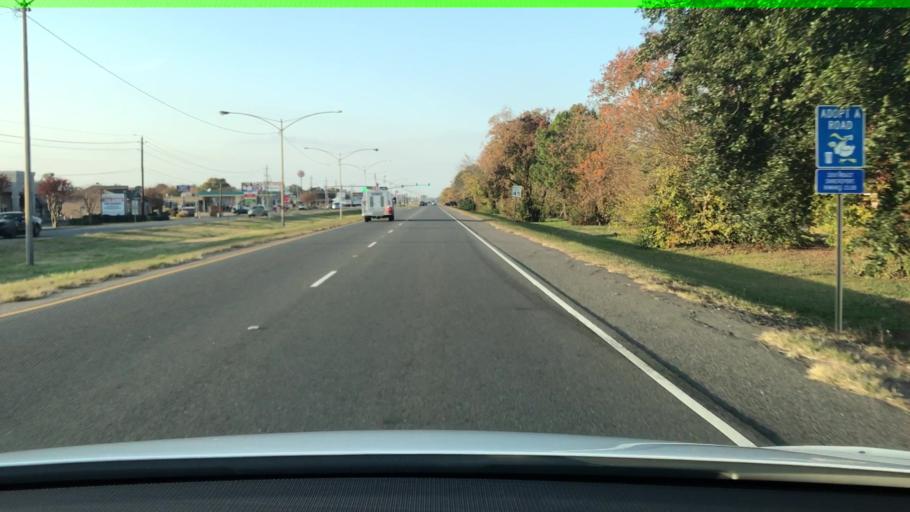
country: US
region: Louisiana
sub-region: Bossier Parish
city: Bossier City
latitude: 32.4185
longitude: -93.7040
